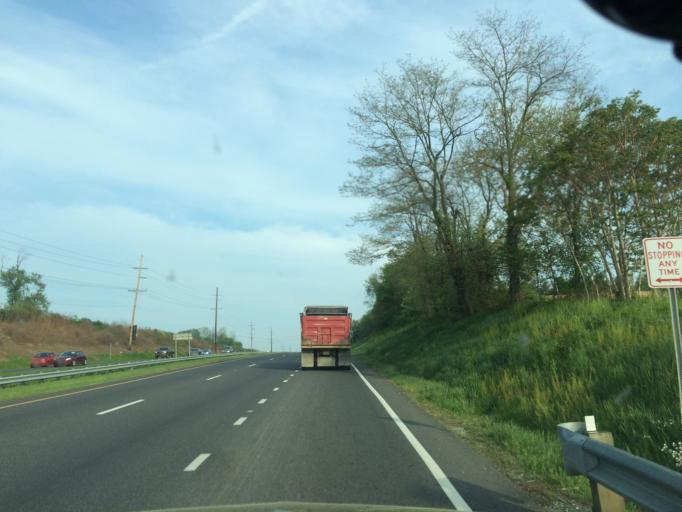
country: US
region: Maryland
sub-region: Carroll County
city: Westminster
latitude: 39.5476
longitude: -76.9421
